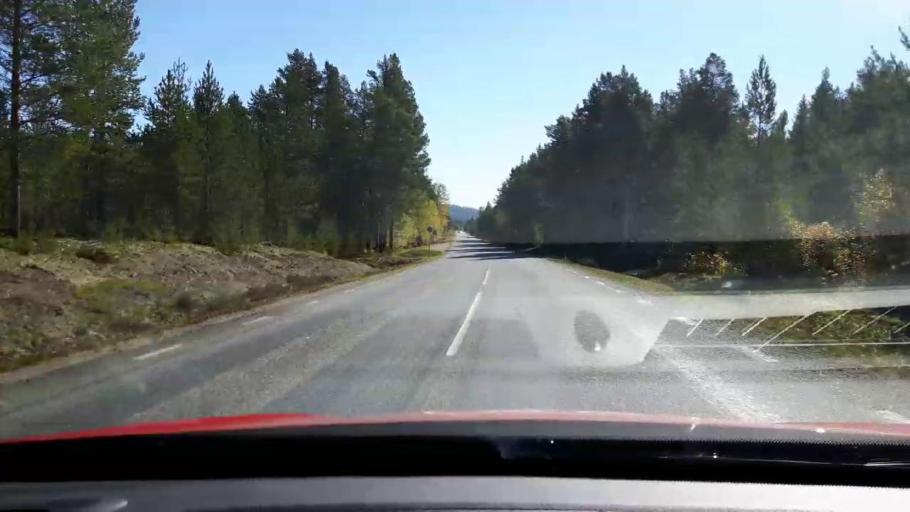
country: SE
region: Jaemtland
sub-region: Harjedalens Kommun
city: Sveg
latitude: 62.3582
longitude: 14.0102
